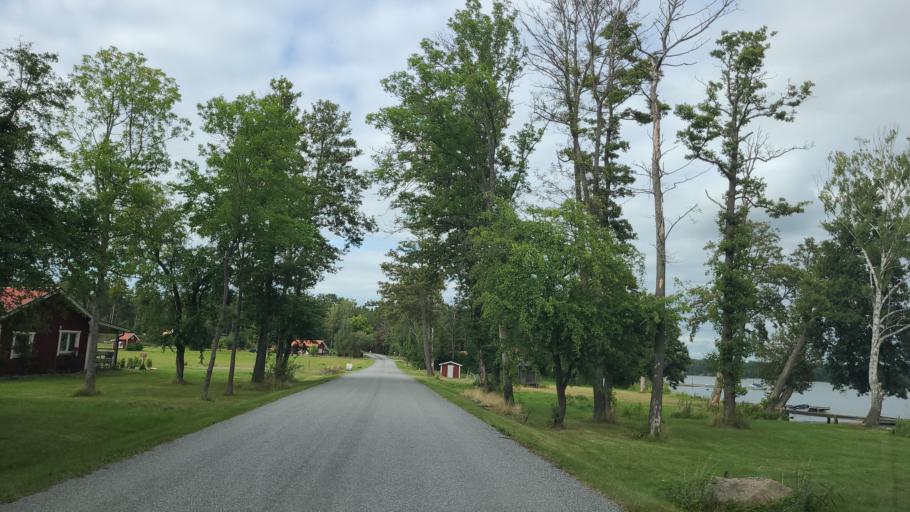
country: SE
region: Stockholm
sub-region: Upplands-Bro Kommun
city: Bro
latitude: 59.4826
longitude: 17.5674
